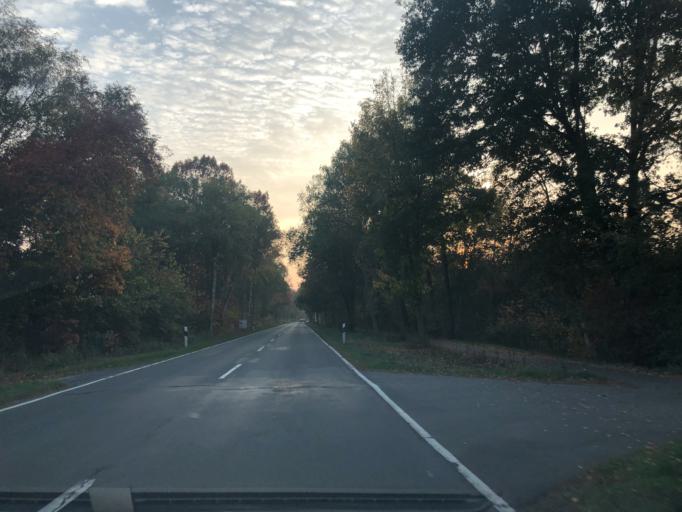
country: DE
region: Lower Saxony
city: Wardenburg
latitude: 53.0432
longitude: 8.1215
